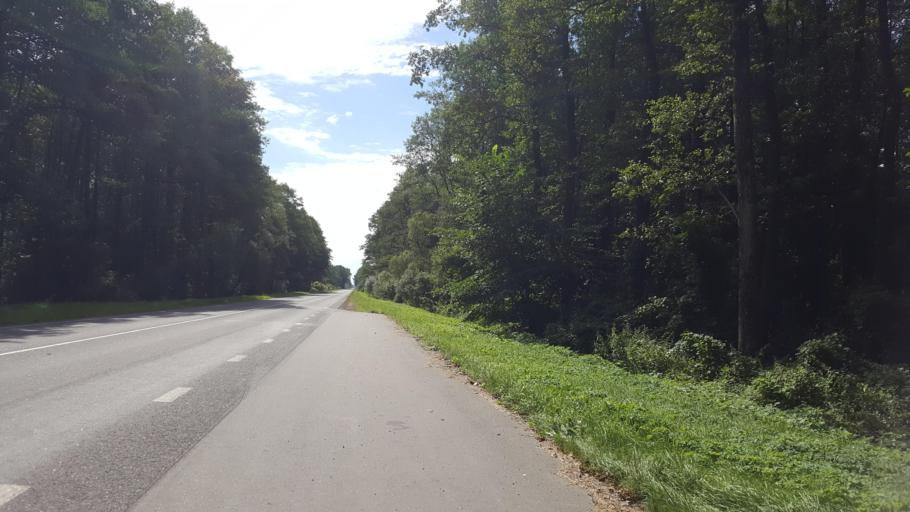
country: BY
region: Brest
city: Zhabinka
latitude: 52.2845
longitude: 23.9455
